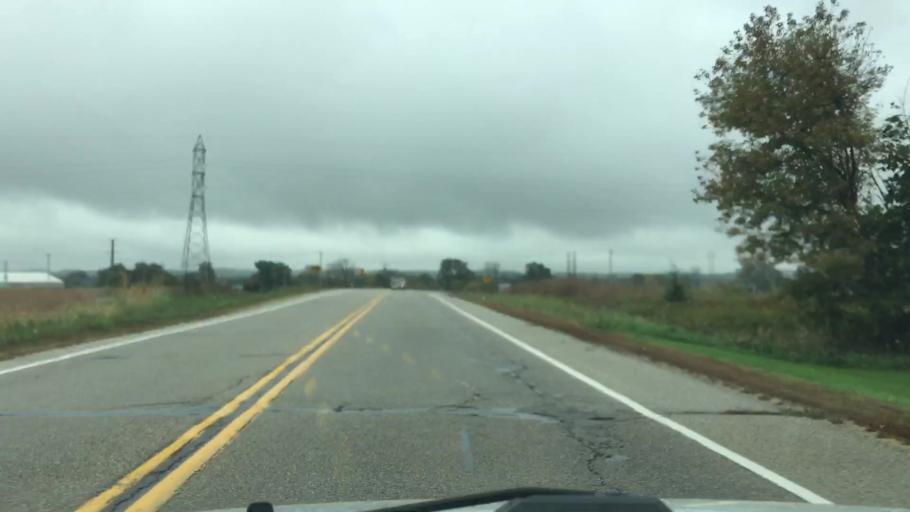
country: US
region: Wisconsin
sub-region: Walworth County
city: Whitewater
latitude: 42.8235
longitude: -88.7021
